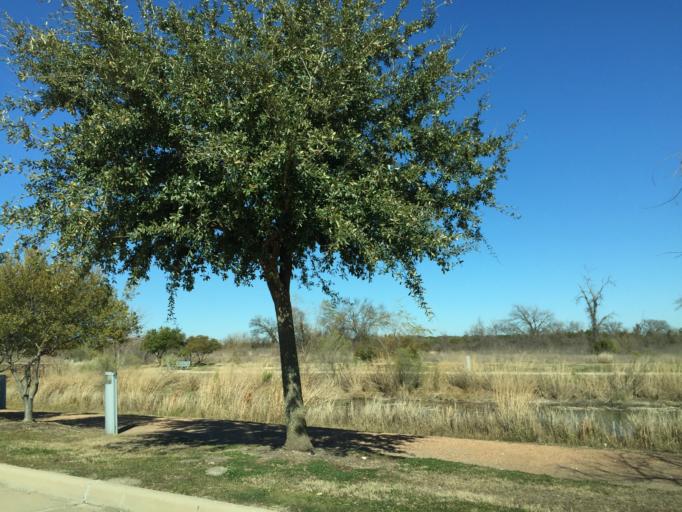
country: US
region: Texas
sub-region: Williamson County
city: Leander
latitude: 30.5873
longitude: -97.8540
